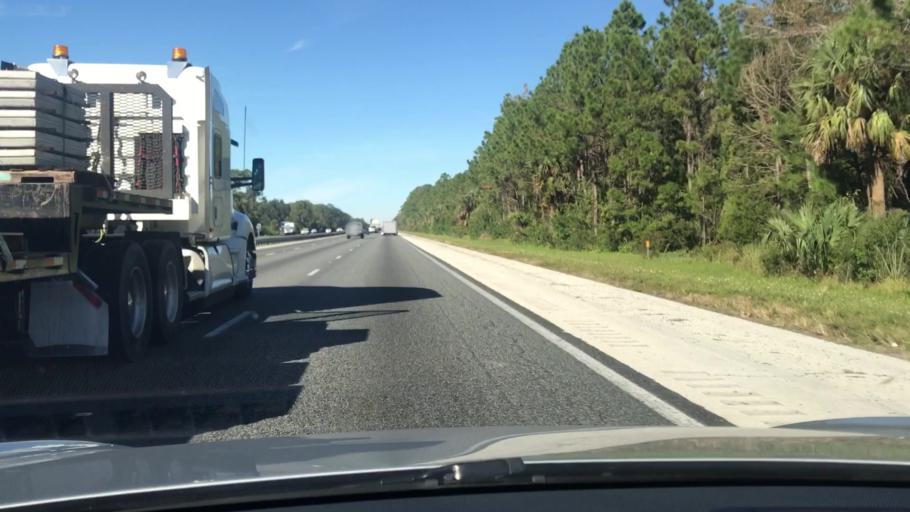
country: US
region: Florida
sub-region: Volusia County
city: Ormond-by-the-Sea
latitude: 29.3642
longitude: -81.1379
